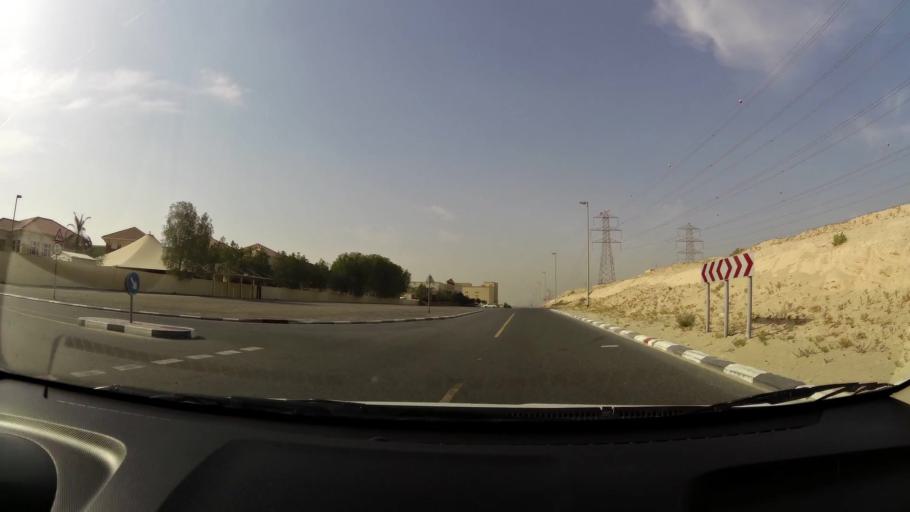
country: AE
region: Ash Shariqah
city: Sharjah
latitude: 25.2421
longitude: 55.4067
